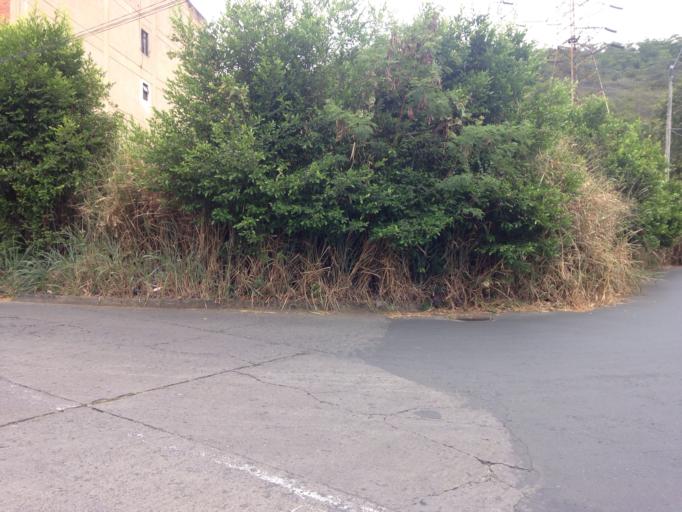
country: CO
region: Valle del Cauca
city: Cali
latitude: 3.4703
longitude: -76.5318
